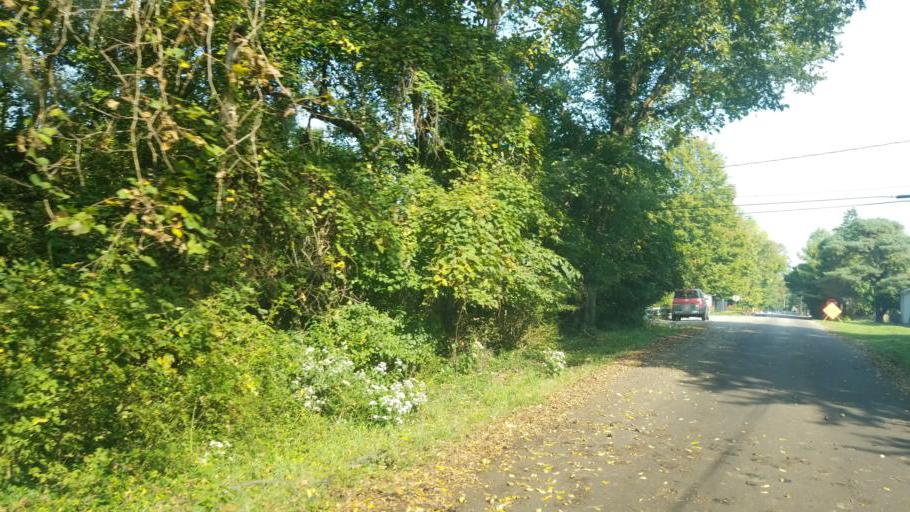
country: US
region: Ohio
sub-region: Franklin County
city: Worthington
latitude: 40.0708
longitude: -83.0297
